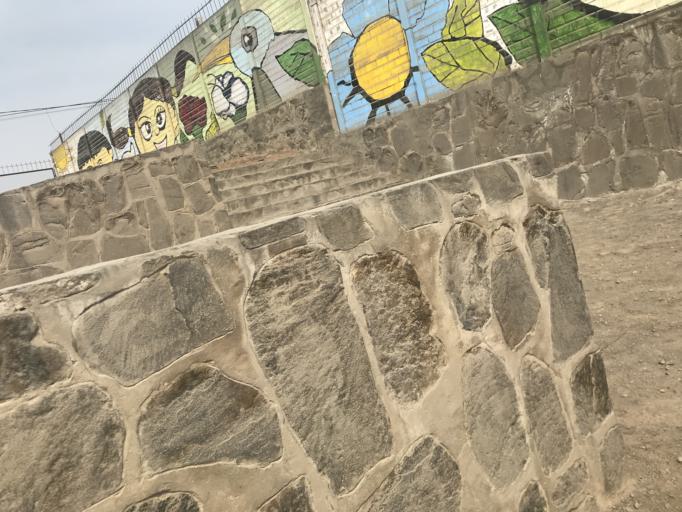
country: PE
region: Lima
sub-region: Lima
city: Carabayllo
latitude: -11.8186
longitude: -77.0437
